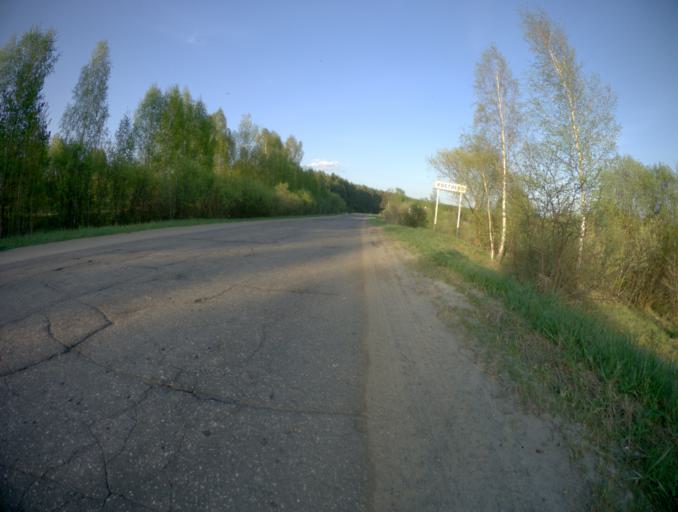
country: RU
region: Ivanovo
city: Yuzha
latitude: 56.5835
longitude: 41.9311
